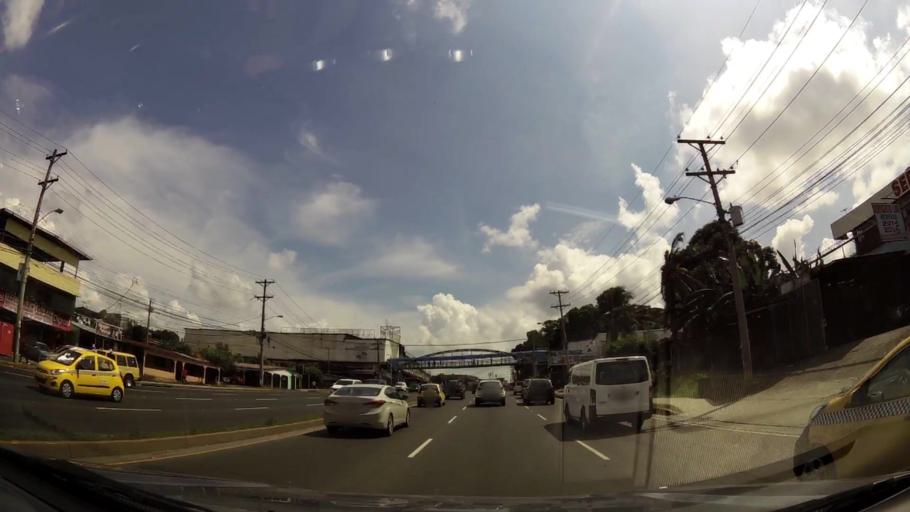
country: PA
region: Panama
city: San Miguelito
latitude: 9.0306
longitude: -79.5033
